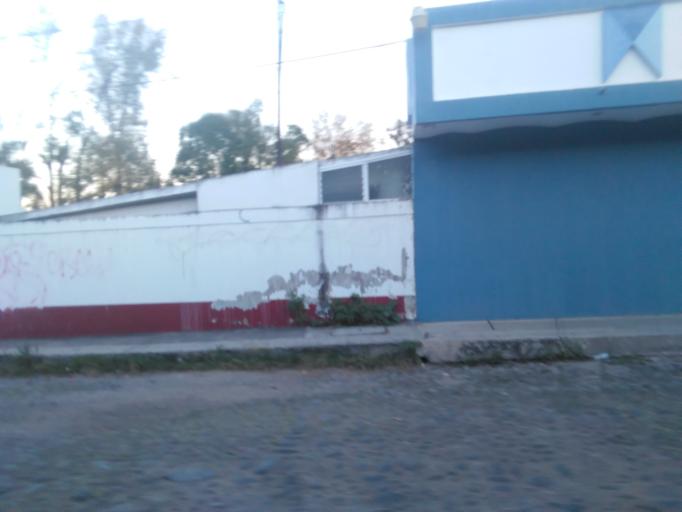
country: MX
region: Nayarit
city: Tepic
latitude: 21.4884
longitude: -104.8933
